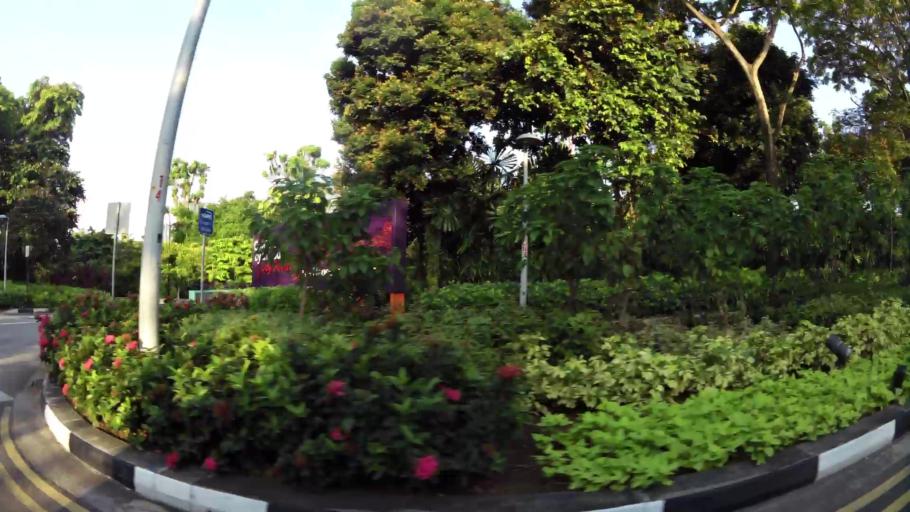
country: SG
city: Singapore
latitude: 1.2776
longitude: 103.8630
